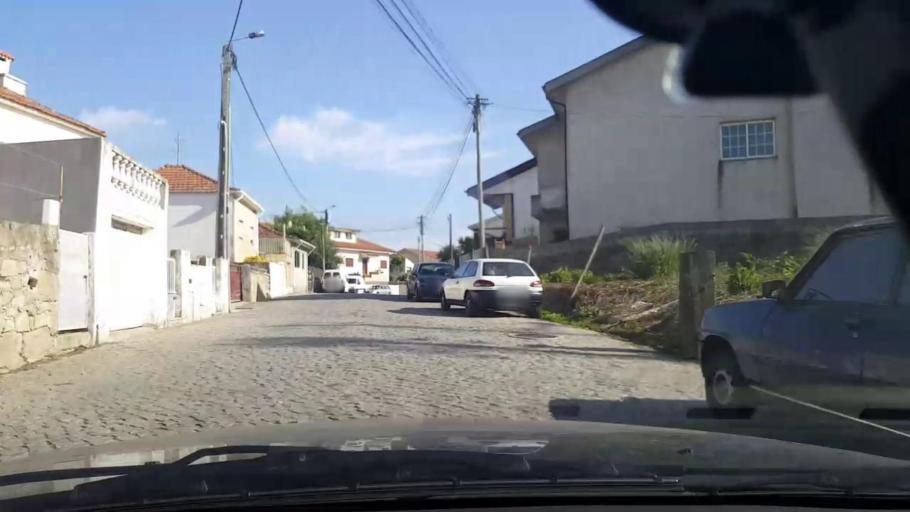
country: PT
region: Porto
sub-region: Maia
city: Gemunde
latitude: 41.2719
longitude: -8.6655
